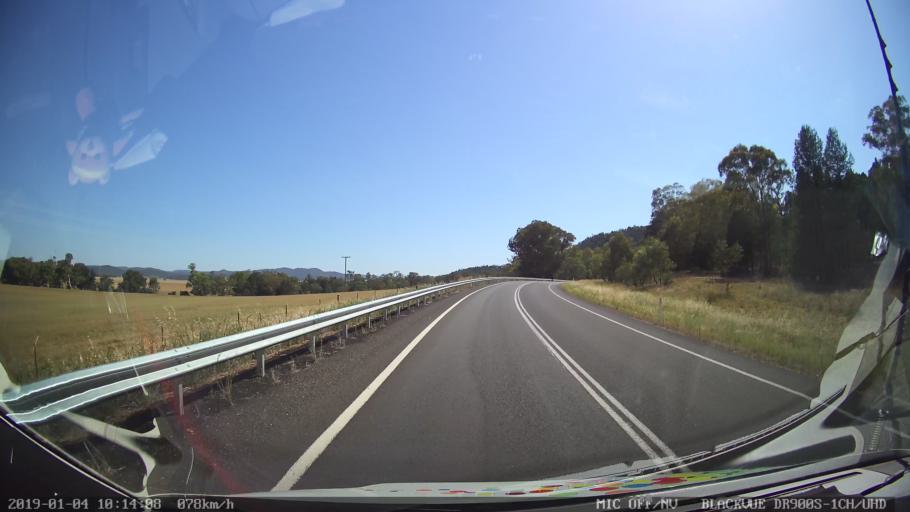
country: AU
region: New South Wales
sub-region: Cabonne
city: Canowindra
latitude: -33.3990
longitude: 148.4100
